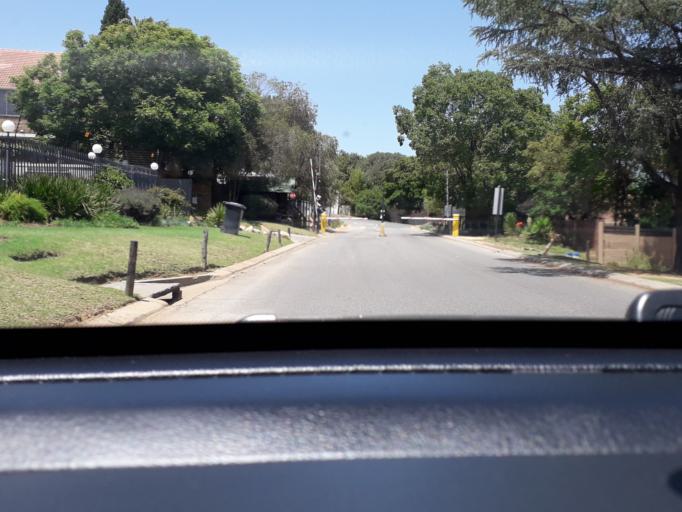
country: ZA
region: Gauteng
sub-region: City of Johannesburg Metropolitan Municipality
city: Modderfontein
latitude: -26.0684
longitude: 28.0705
